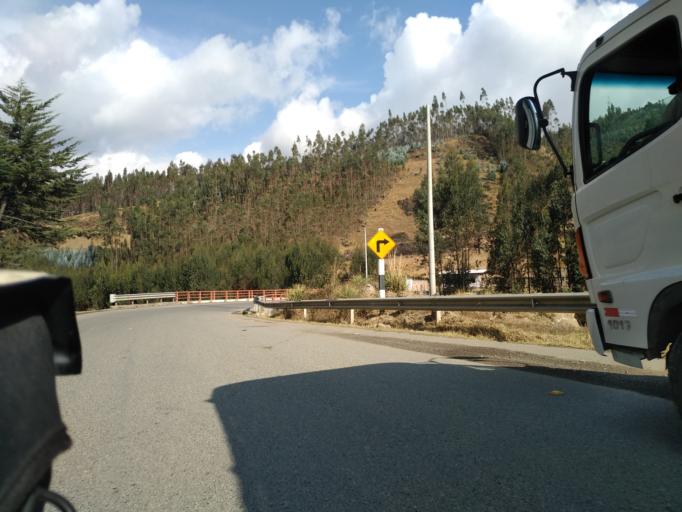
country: PE
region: La Libertad
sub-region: Provincia de Otuzco
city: Mache
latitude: -7.9984
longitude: -78.5069
